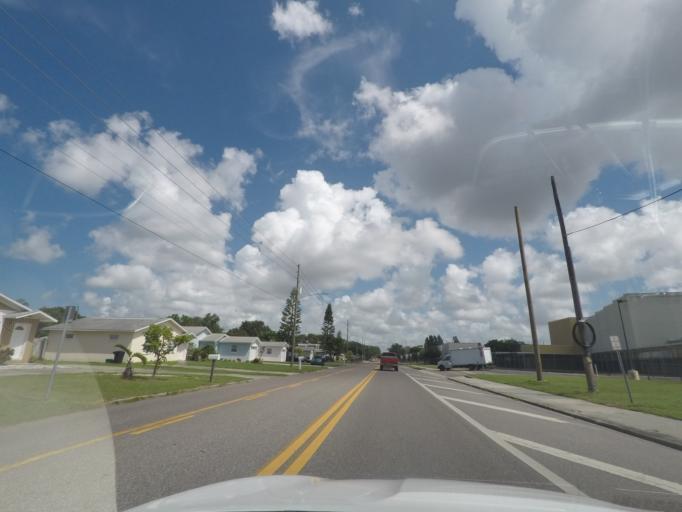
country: US
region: Florida
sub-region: Pinellas County
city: Gulfport
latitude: 27.7612
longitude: -82.7121
